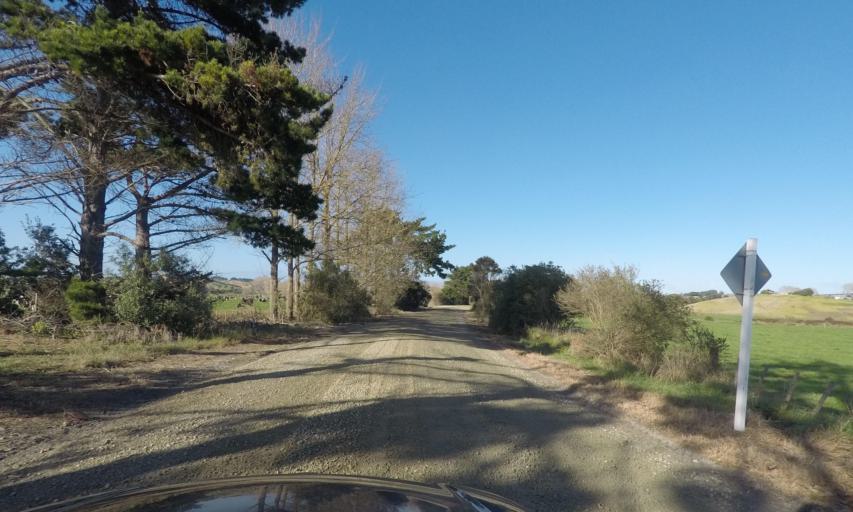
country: NZ
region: Auckland
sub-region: Auckland
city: Wellsford
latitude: -36.1486
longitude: 174.6064
